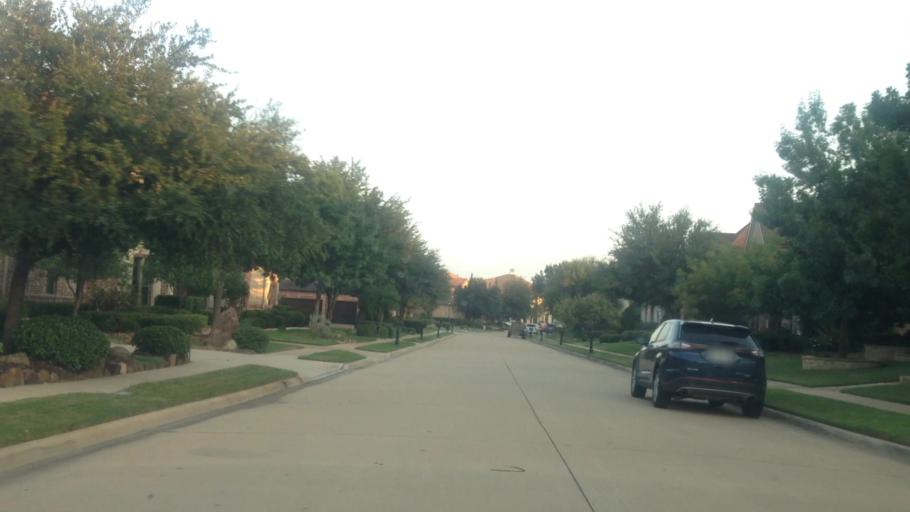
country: US
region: Texas
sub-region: Denton County
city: The Colony
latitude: 33.1246
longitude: -96.8792
